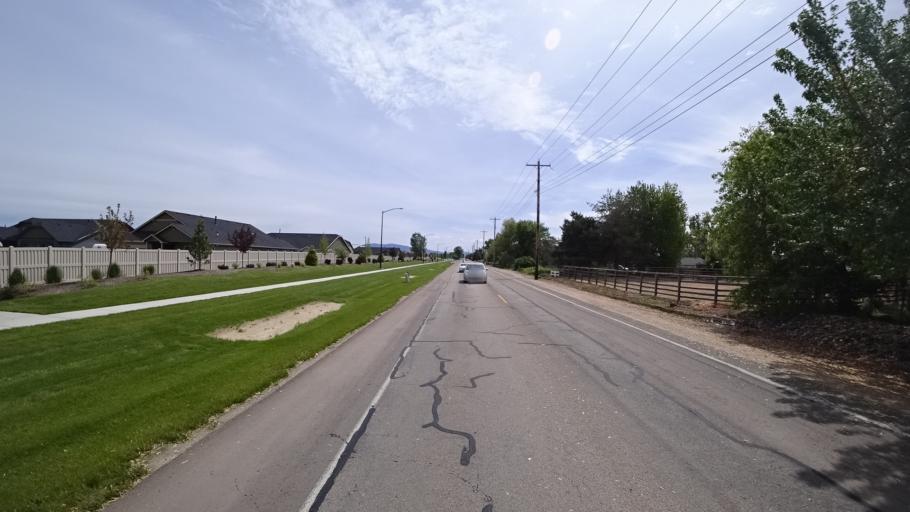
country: US
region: Idaho
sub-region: Ada County
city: Meridian
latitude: 43.5612
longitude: -116.3687
